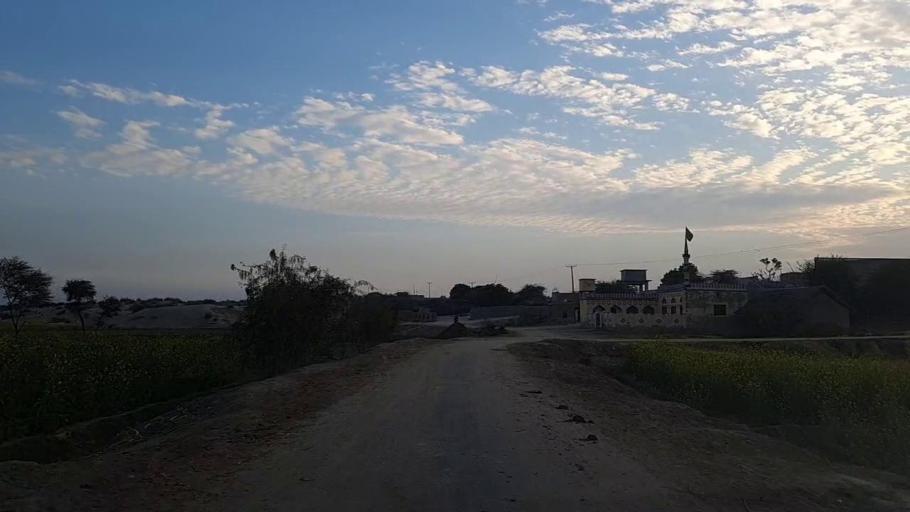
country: PK
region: Sindh
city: Daur
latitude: 26.4130
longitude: 68.4678
